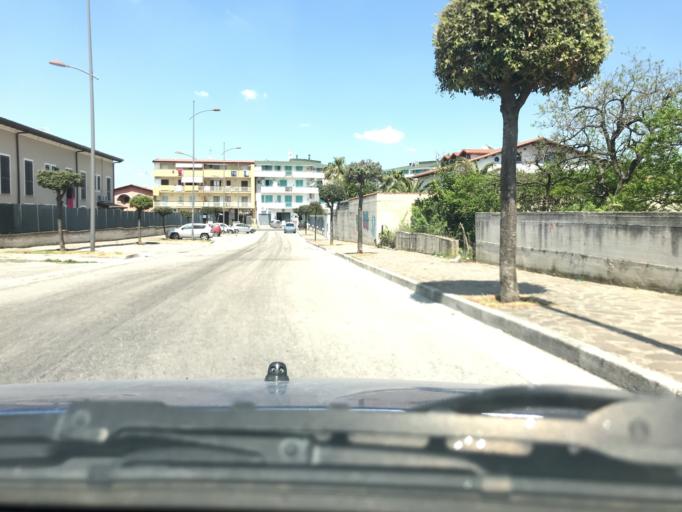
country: IT
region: Campania
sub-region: Provincia di Napoli
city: Villaricca
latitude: 40.9176
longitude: 14.1766
